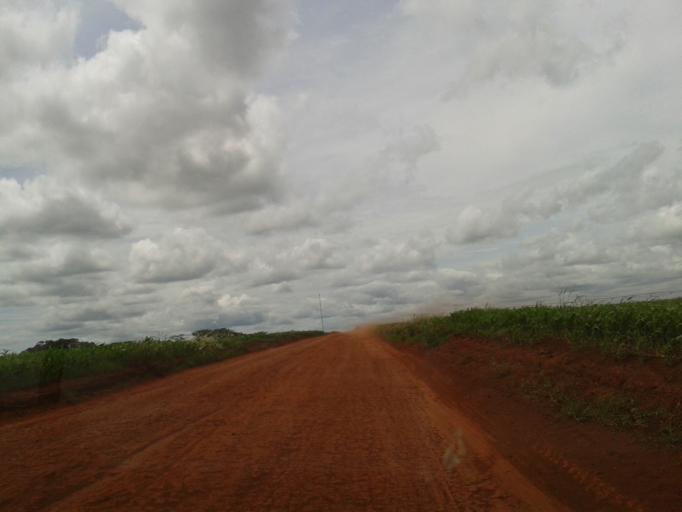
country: BR
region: Minas Gerais
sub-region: Centralina
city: Centralina
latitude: -18.5946
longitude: -49.2283
